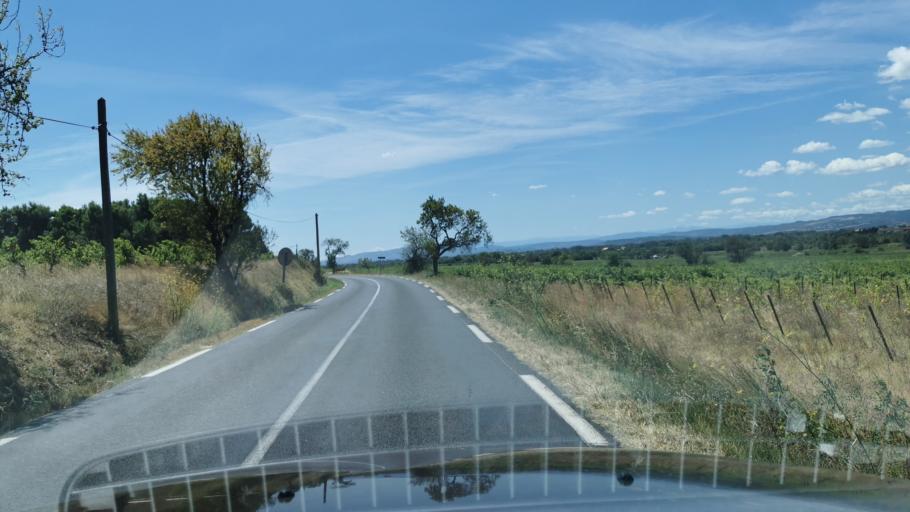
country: FR
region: Languedoc-Roussillon
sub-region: Departement de l'Aude
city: Vinassan
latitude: 43.1848
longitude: 3.0643
